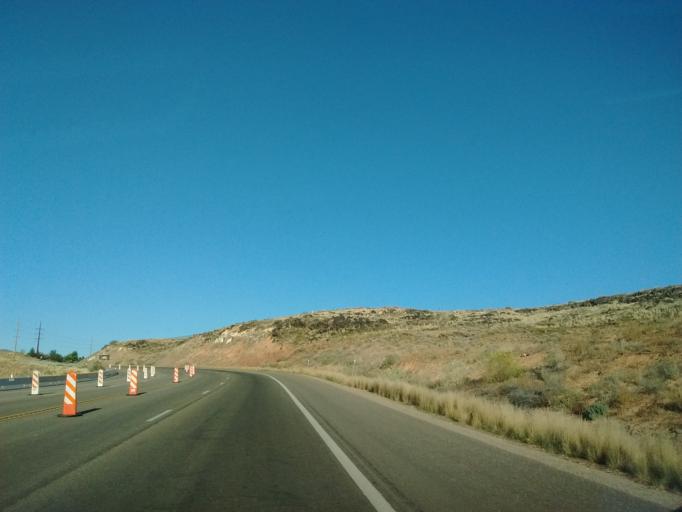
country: US
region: Utah
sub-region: Washington County
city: Washington
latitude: 37.1361
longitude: -113.4752
